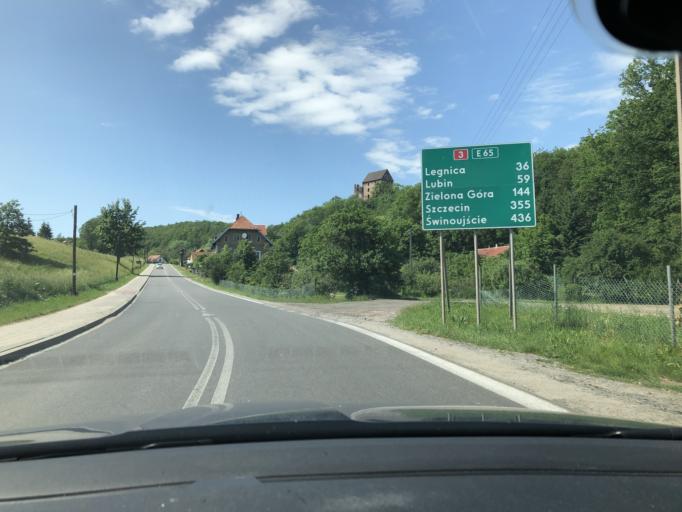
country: PL
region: Lower Silesian Voivodeship
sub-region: Powiat jaworski
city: Bolkow
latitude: 50.9355
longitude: 16.1137
